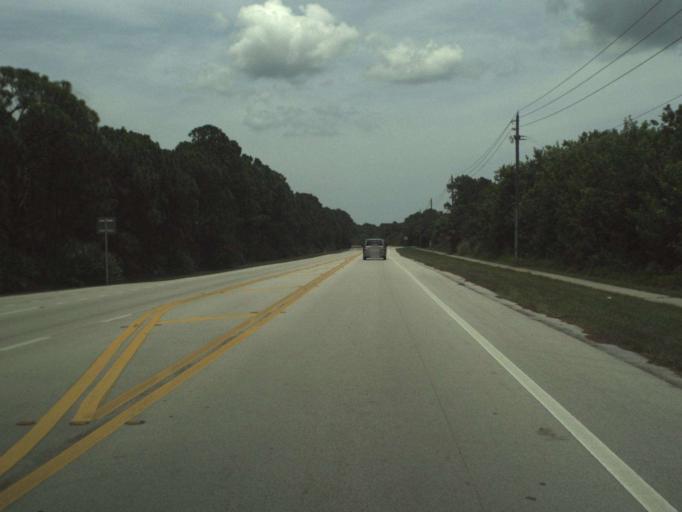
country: US
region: Florida
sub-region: Saint Lucie County
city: Lakewood Park
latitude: 27.5381
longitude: -80.3825
